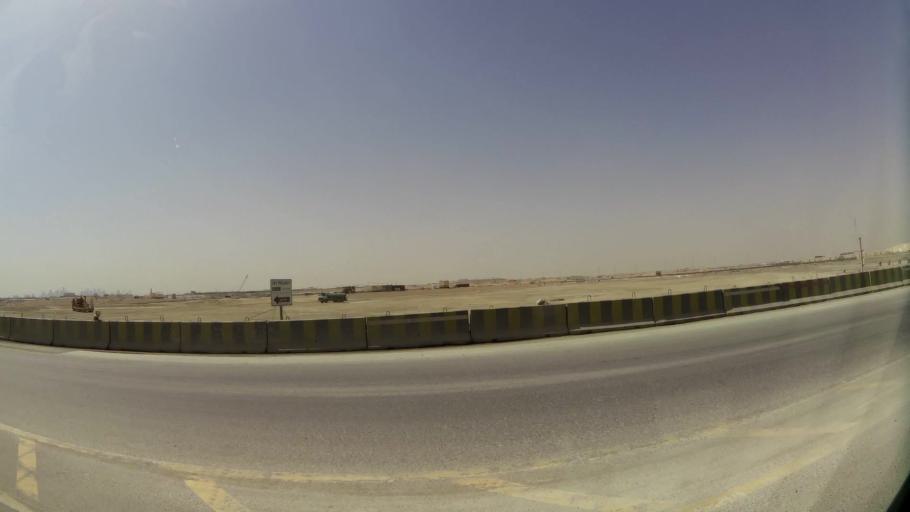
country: QA
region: Baladiyat Umm Salal
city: Umm Salal Muhammad
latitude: 25.4059
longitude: 51.4953
